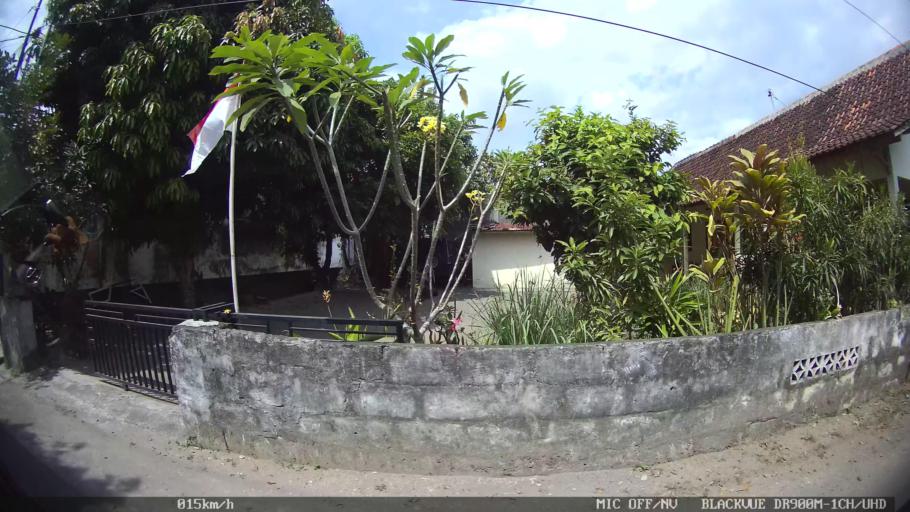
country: ID
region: Daerah Istimewa Yogyakarta
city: Gamping Lor
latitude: -7.8078
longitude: 110.3370
